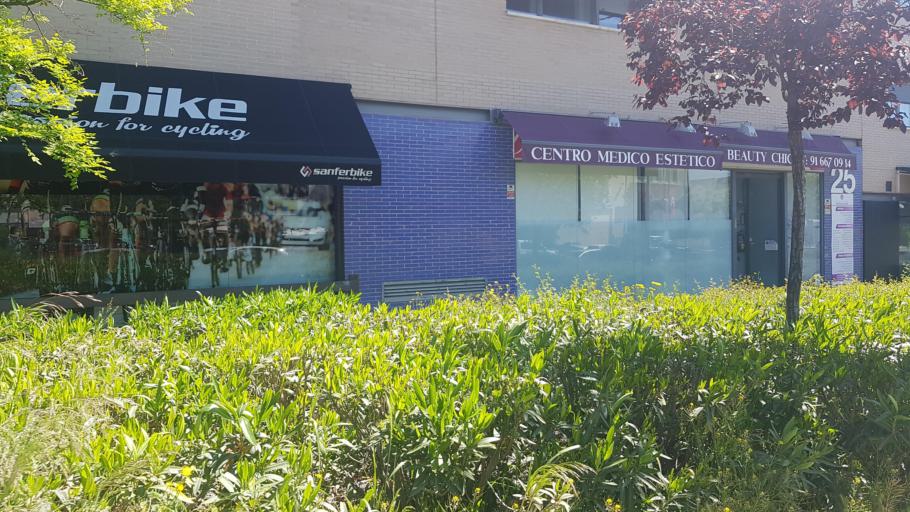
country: ES
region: Madrid
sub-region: Provincia de Madrid
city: San Sebastian de los Reyes
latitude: 40.5602
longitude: -3.6170
